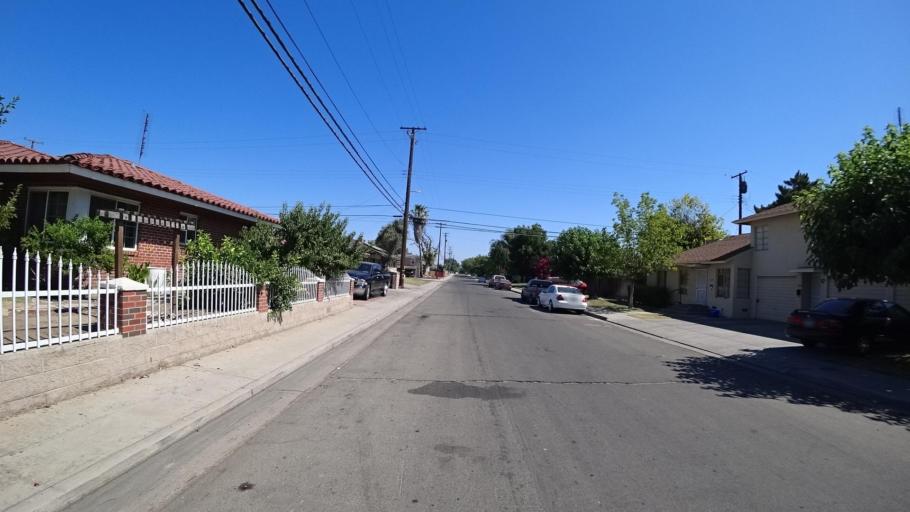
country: US
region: California
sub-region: Fresno County
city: Fresno
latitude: 36.7587
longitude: -119.8200
